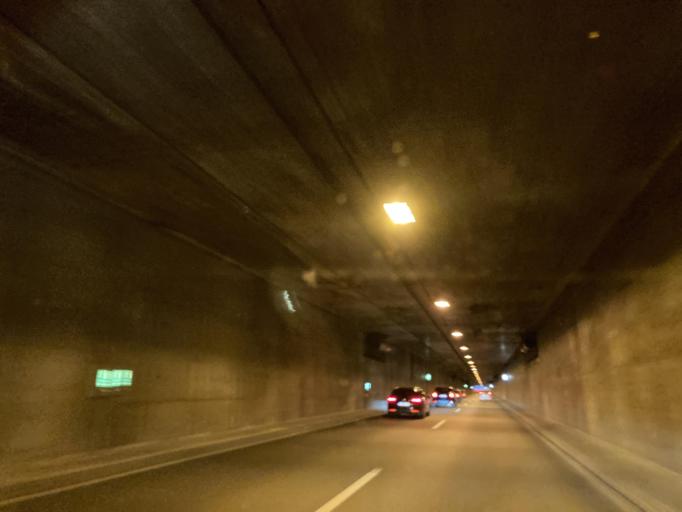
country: DE
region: Baden-Wuerttemberg
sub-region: Freiburg Region
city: Freiburg
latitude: 47.9873
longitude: 7.8673
